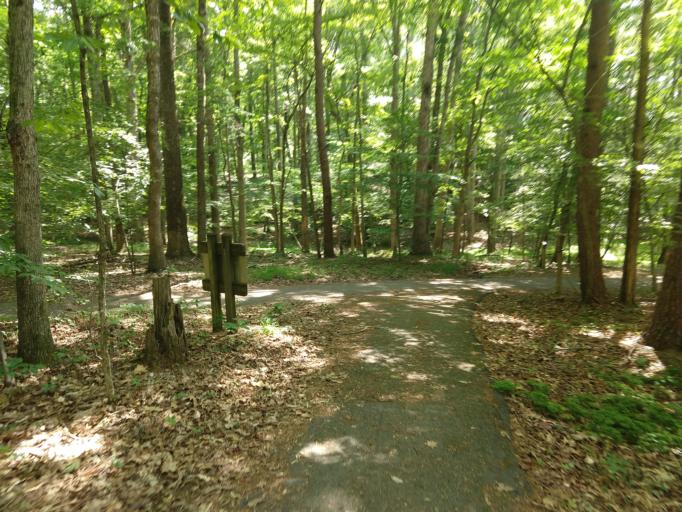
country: US
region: Virginia
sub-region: Louisa County
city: Louisa
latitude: 38.1111
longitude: -77.8305
